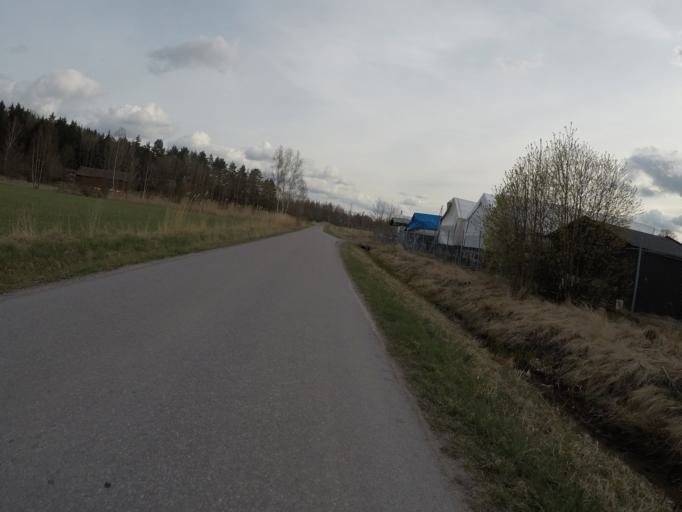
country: SE
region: Soedermanland
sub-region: Eskilstuna Kommun
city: Torshalla
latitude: 59.4279
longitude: 16.4892
